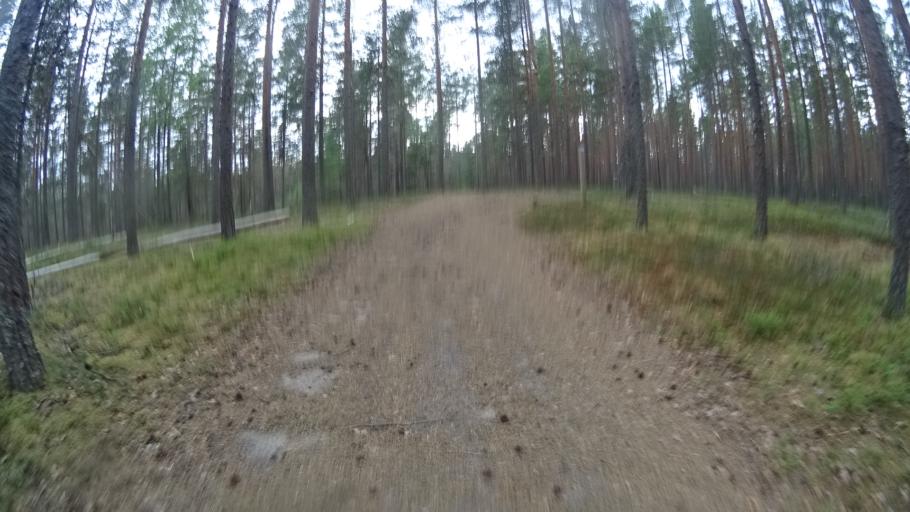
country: FI
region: Satakunta
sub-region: Pohjois-Satakunta
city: Jaemijaervi
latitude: 61.7692
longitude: 22.7593
